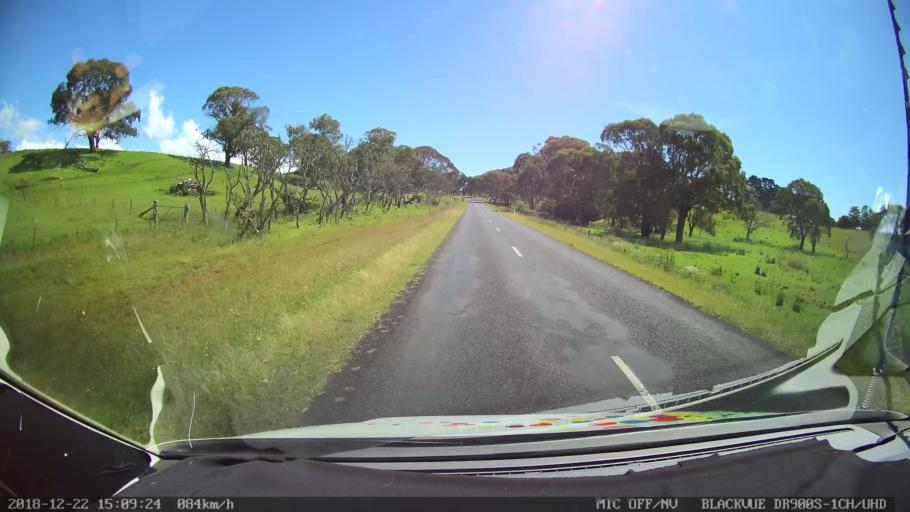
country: AU
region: New South Wales
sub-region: Bellingen
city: Dorrigo
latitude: -30.3237
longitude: 152.4092
